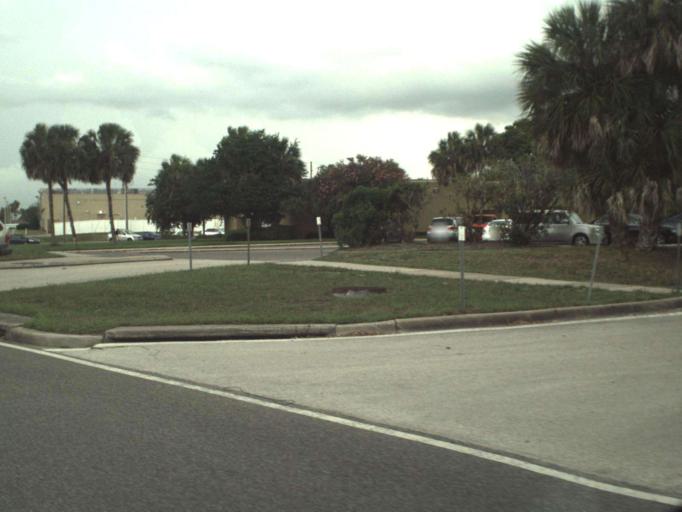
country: US
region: Florida
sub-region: Seminole County
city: Goldenrod
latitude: 28.6301
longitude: -81.3182
